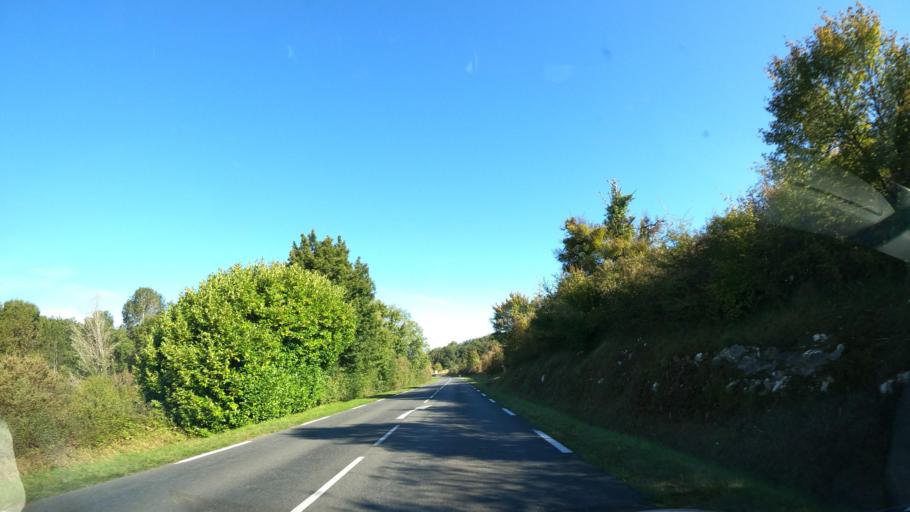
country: FR
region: Aquitaine
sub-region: Departement de la Dordogne
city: Lembras
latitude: 44.9009
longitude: 0.5567
